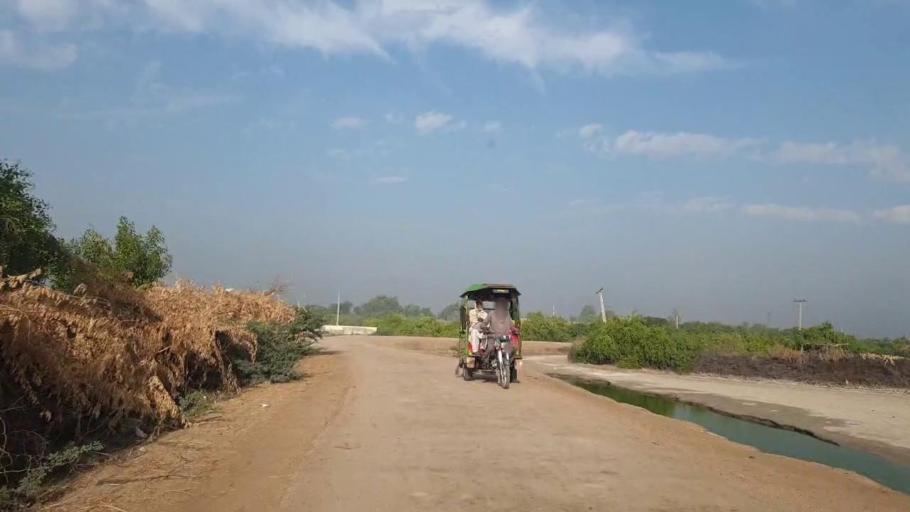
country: PK
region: Sindh
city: Tando Bago
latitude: 24.8217
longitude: 68.9750
